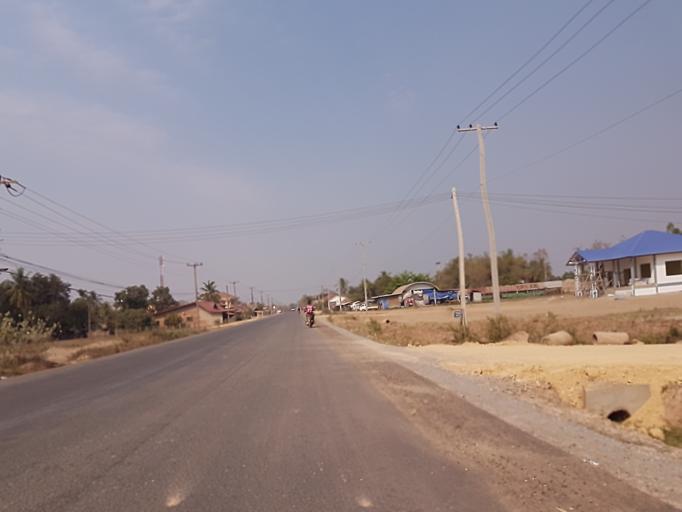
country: TH
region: Nong Khai
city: Nong Khai
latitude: 17.9196
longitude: 102.7673
